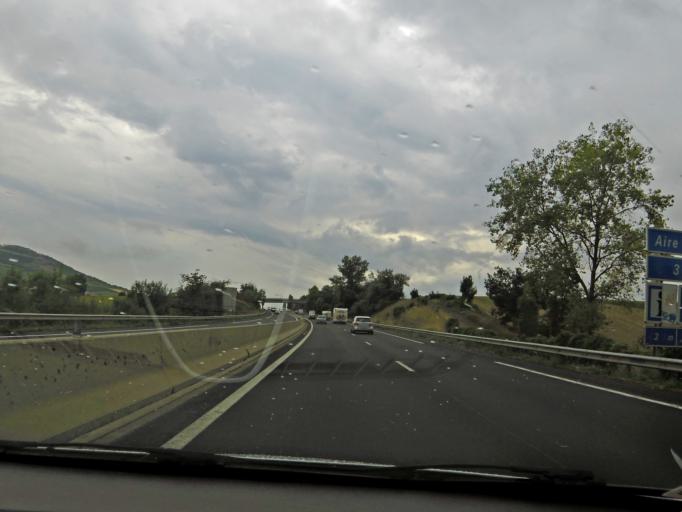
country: FR
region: Auvergne
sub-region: Departement du Puy-de-Dome
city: Tallende
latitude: 45.6642
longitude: 3.1470
